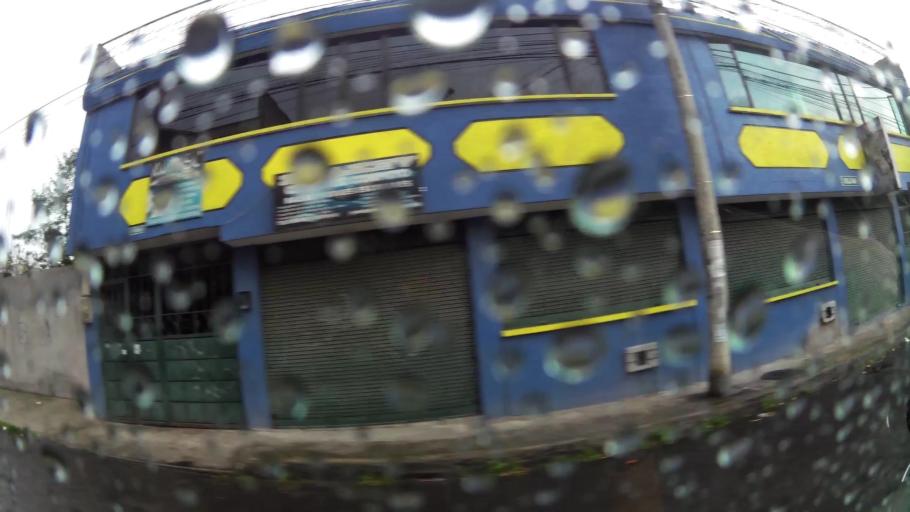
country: EC
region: Pichincha
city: Quito
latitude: -0.3093
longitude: -78.5478
